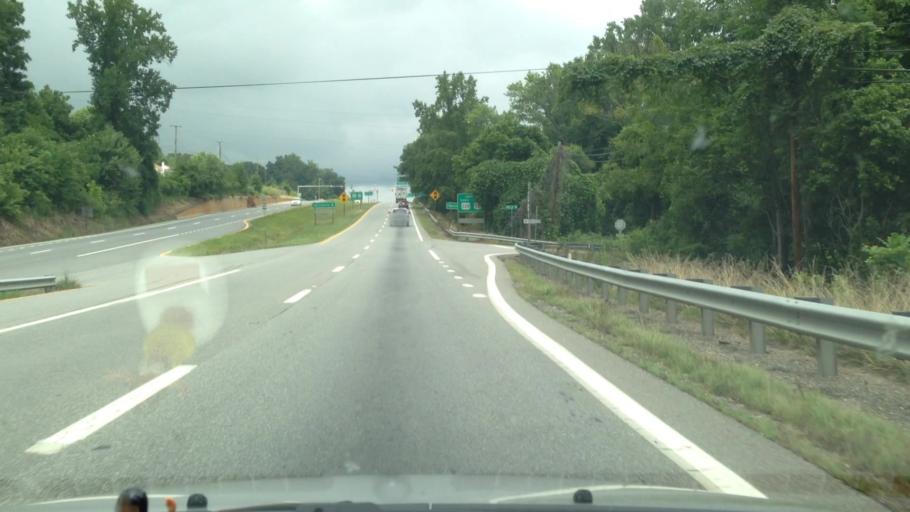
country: US
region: Virginia
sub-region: Henry County
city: Chatmoss
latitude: 36.6184
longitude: -79.8603
